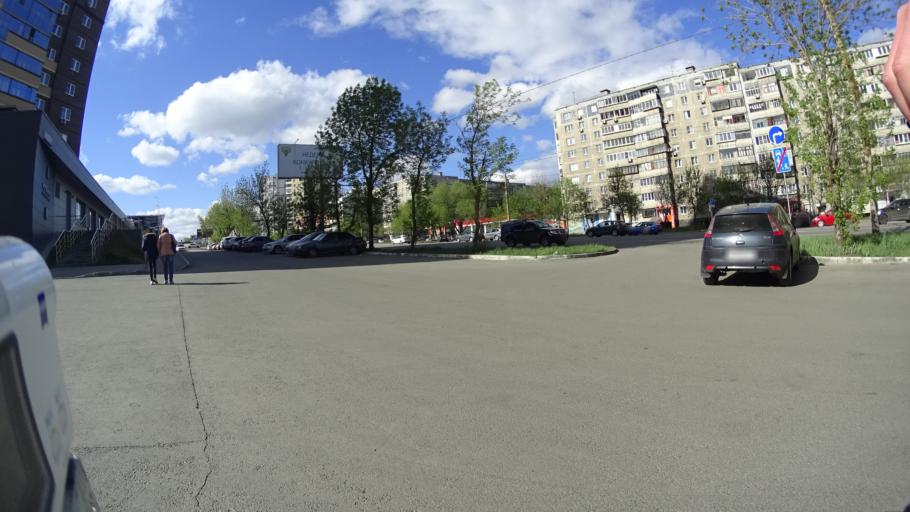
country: RU
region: Chelyabinsk
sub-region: Gorod Chelyabinsk
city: Chelyabinsk
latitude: 55.1789
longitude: 61.2968
